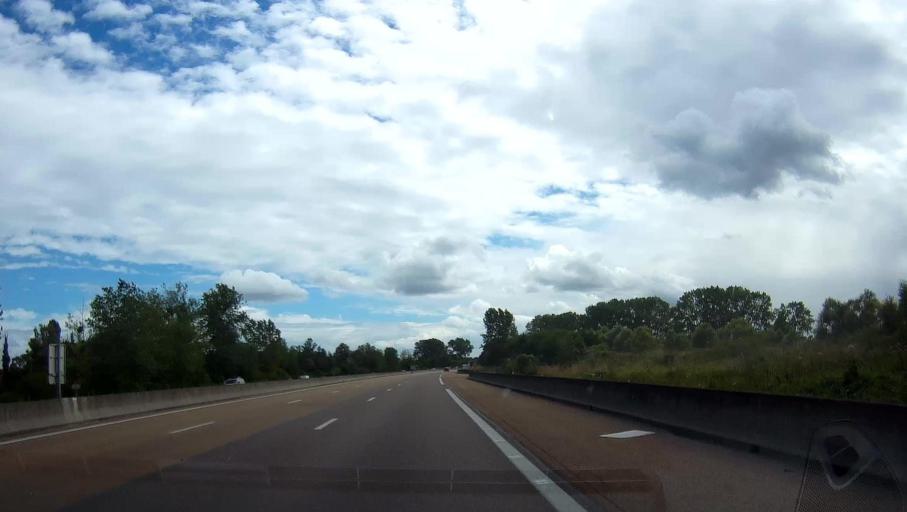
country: FR
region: Bourgogne
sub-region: Departement de la Cote-d'Or
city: Saint-Julien
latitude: 47.4077
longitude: 5.1805
